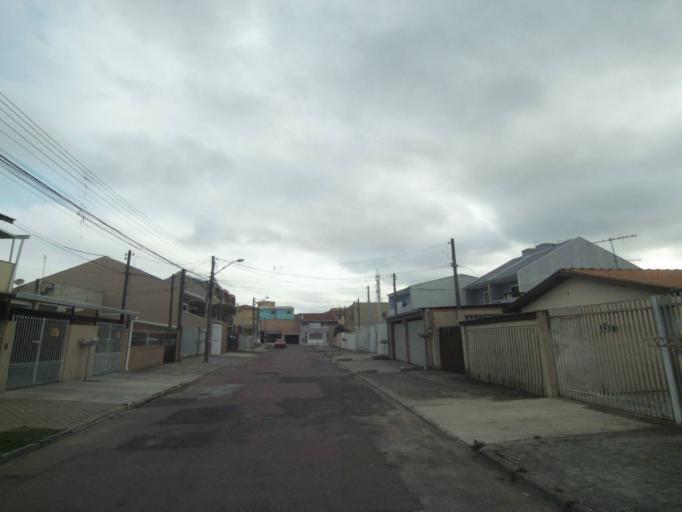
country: BR
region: Parana
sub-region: Sao Jose Dos Pinhais
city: Sao Jose dos Pinhais
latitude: -25.5477
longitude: -49.2575
